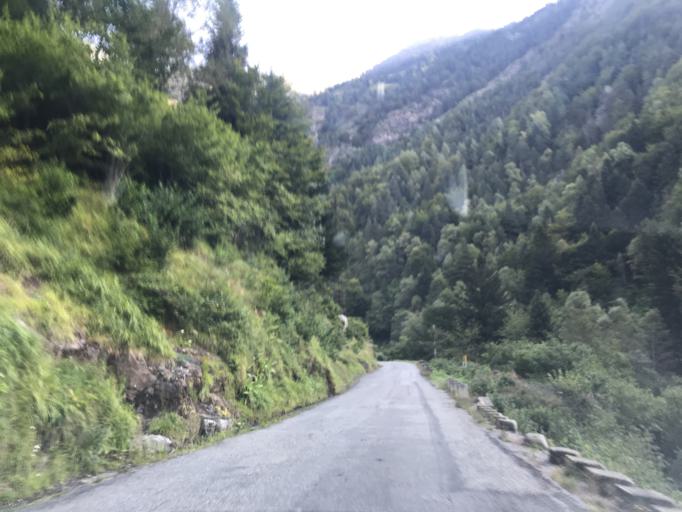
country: FR
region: Midi-Pyrenees
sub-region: Departement des Hautes-Pyrenees
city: Saint-Lary-Soulan
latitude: 42.7981
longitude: 0.2277
